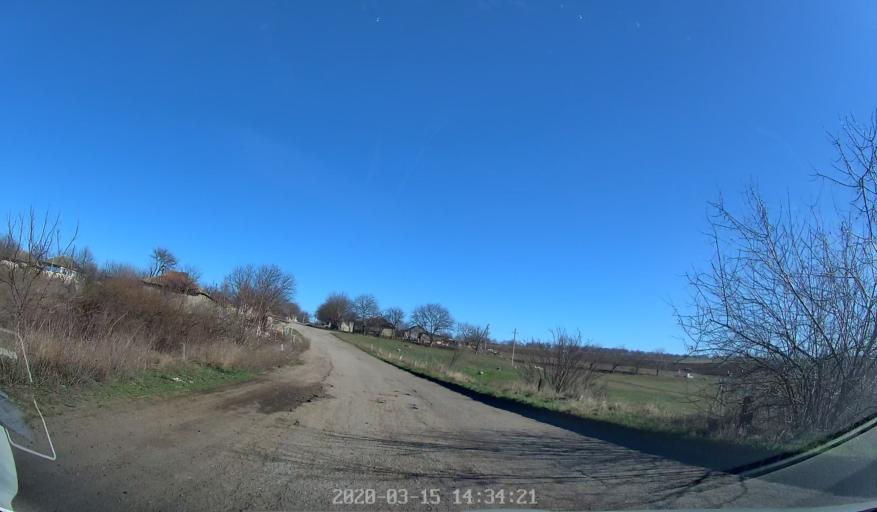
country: MD
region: Orhei
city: Orhei
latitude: 47.3323
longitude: 28.9186
